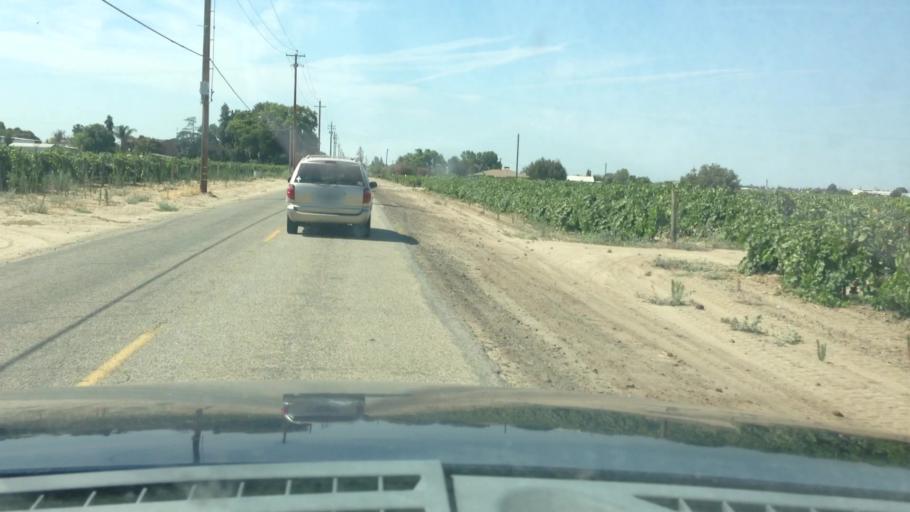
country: US
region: California
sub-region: Fresno County
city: Kingsburg
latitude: 36.5406
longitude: -119.5566
